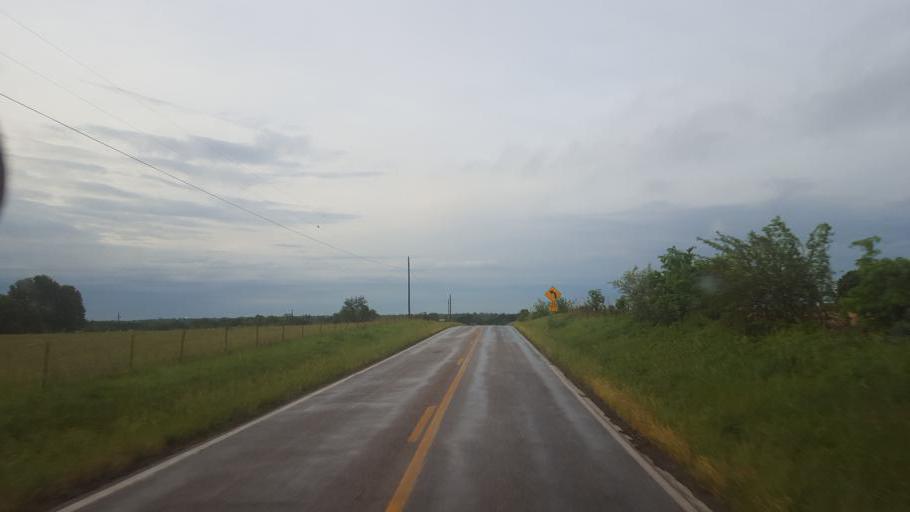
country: US
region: Missouri
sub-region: Moniteau County
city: California
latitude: 38.6739
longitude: -92.5865
